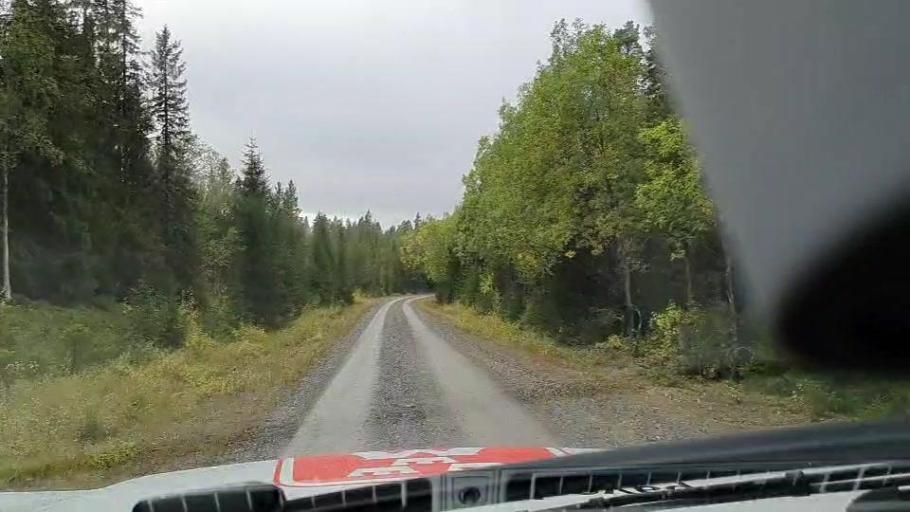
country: SE
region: Jaemtland
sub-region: Are Kommun
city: Jarpen
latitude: 63.2027
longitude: 13.2811
